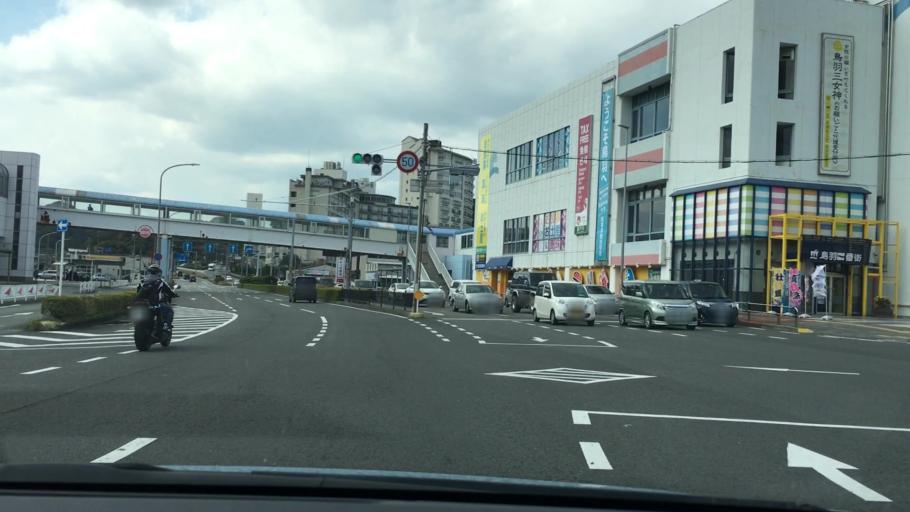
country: JP
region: Mie
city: Toba
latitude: 34.4867
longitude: 136.8442
